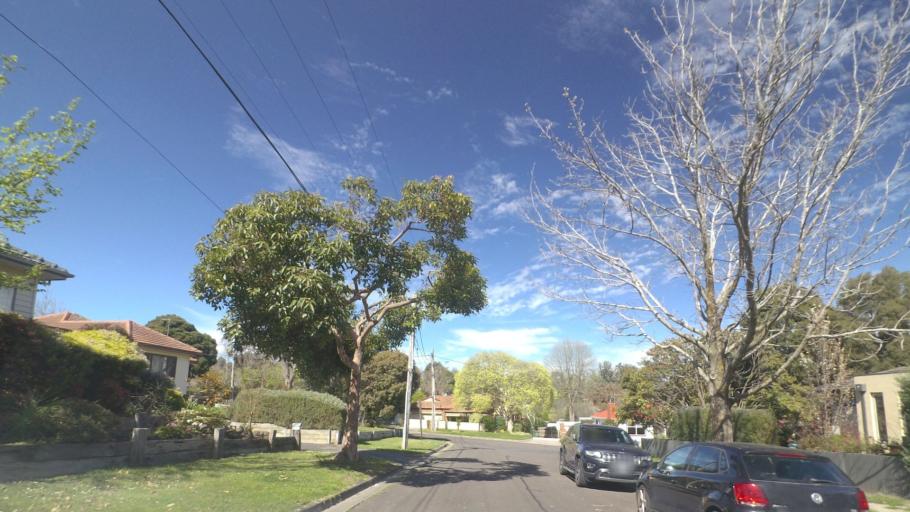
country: AU
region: Victoria
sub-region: Maroondah
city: Ringwood East
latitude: -37.8163
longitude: 145.2486
